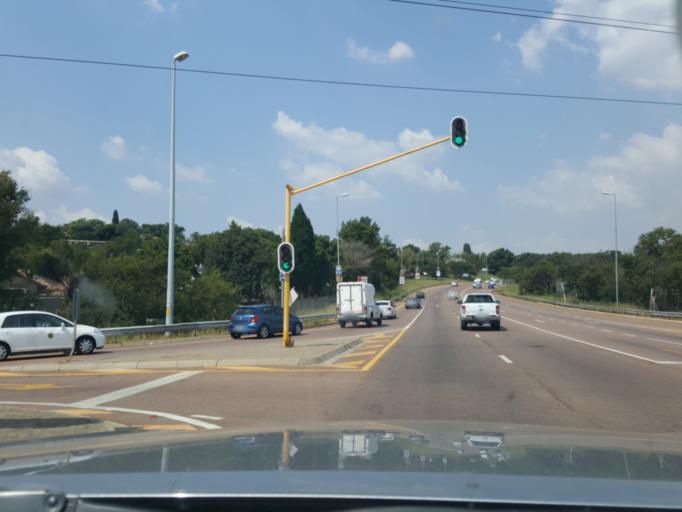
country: ZA
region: Gauteng
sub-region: City of Tshwane Metropolitan Municipality
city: Centurion
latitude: -25.8142
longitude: 28.2348
